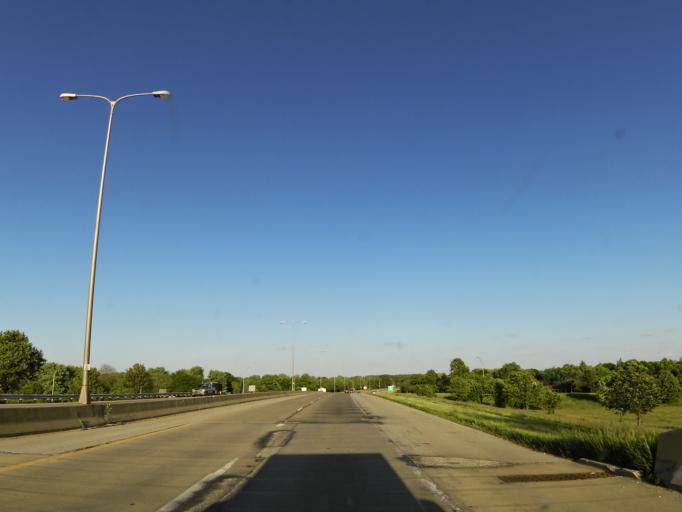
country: US
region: Illinois
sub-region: Champaign County
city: Urbana
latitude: 40.1337
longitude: -88.1955
